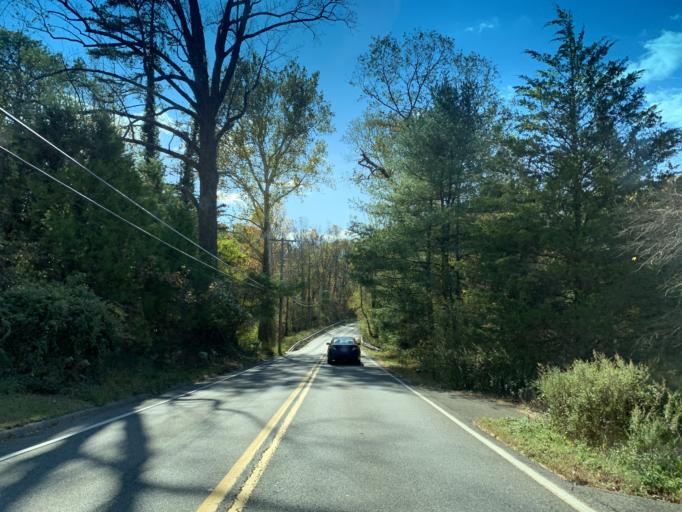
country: US
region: Maryland
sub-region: Anne Arundel County
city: Gambrills
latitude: 39.0912
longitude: -76.6538
